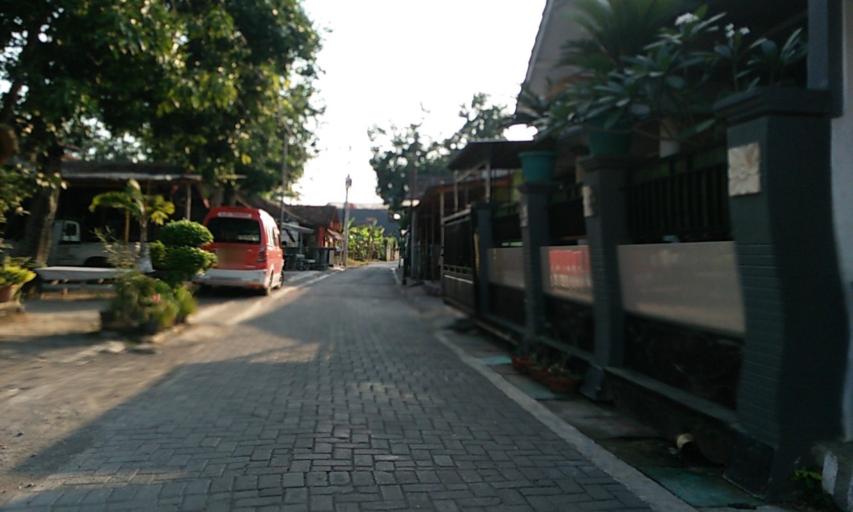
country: ID
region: Central Java
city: Mranggen
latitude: -7.0120
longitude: 110.4888
